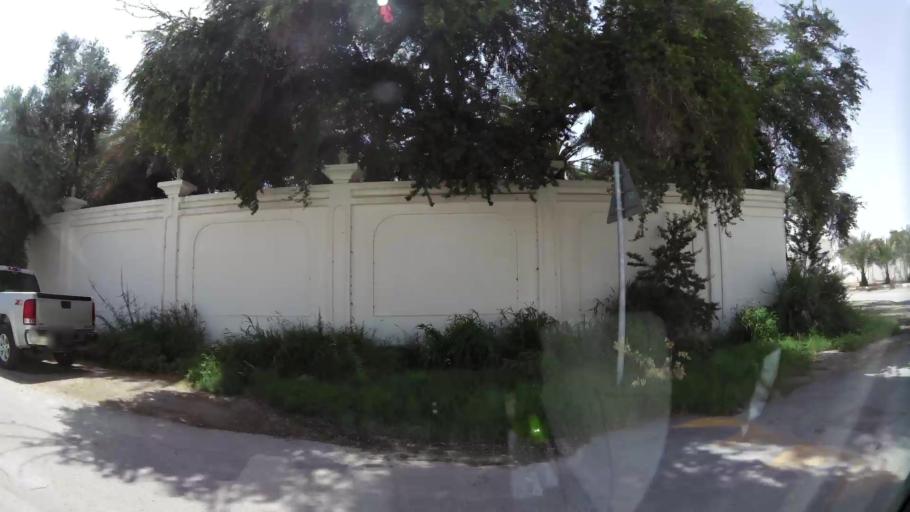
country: QA
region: Baladiyat Umm Salal
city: Umm Salal Muhammad
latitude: 25.3718
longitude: 51.4308
